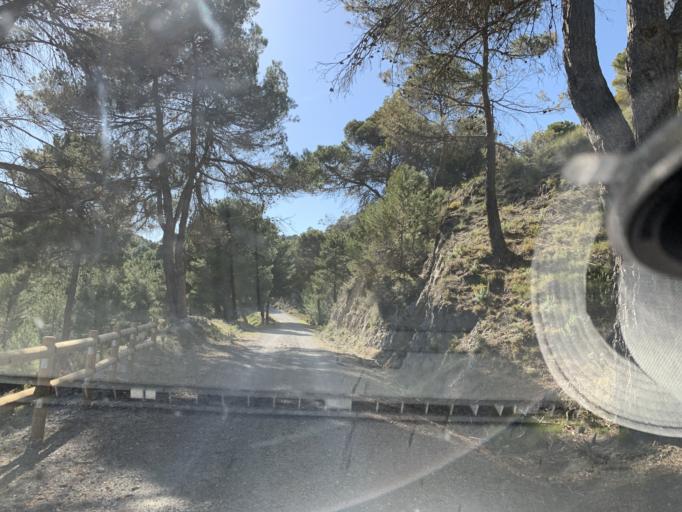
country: ES
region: Andalusia
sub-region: Provincia de Granada
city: Beas de Granada
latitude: 37.2347
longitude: -3.4311
